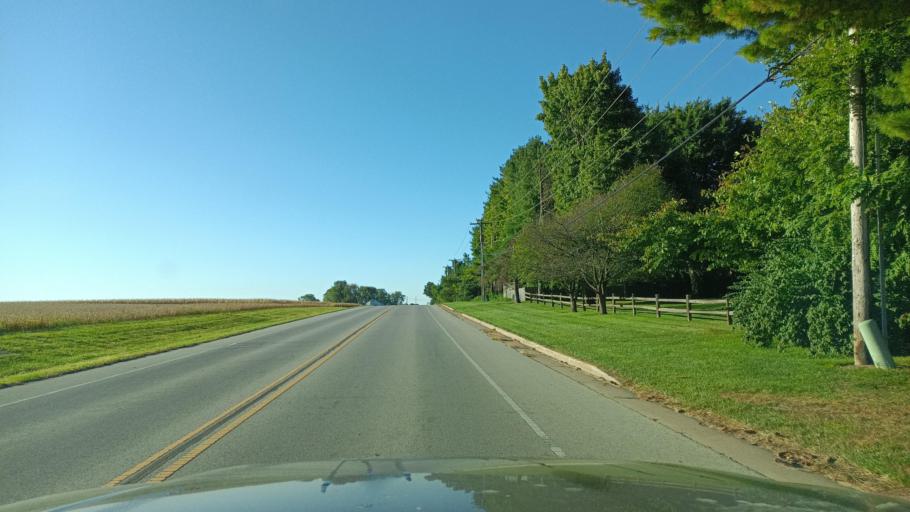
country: US
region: Illinois
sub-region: Champaign County
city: Savoy
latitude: 40.0648
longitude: -88.2384
